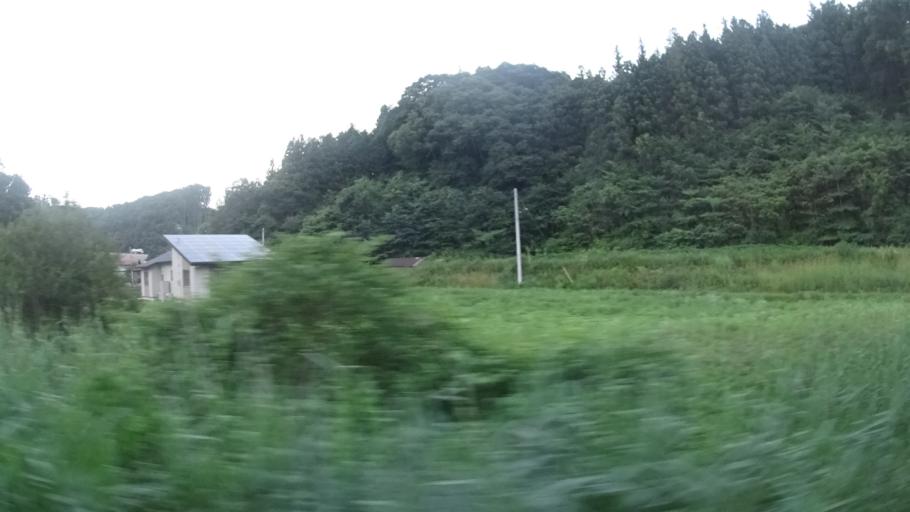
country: JP
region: Fukushima
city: Funehikimachi-funehiki
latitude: 37.2910
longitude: 140.6351
